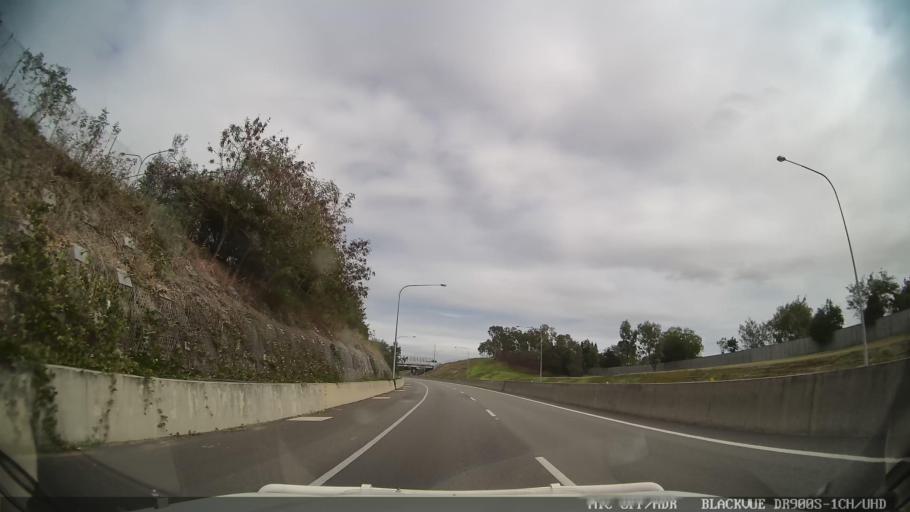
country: AU
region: Queensland
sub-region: Townsville
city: Bohle Plains
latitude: -19.3213
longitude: 146.7442
